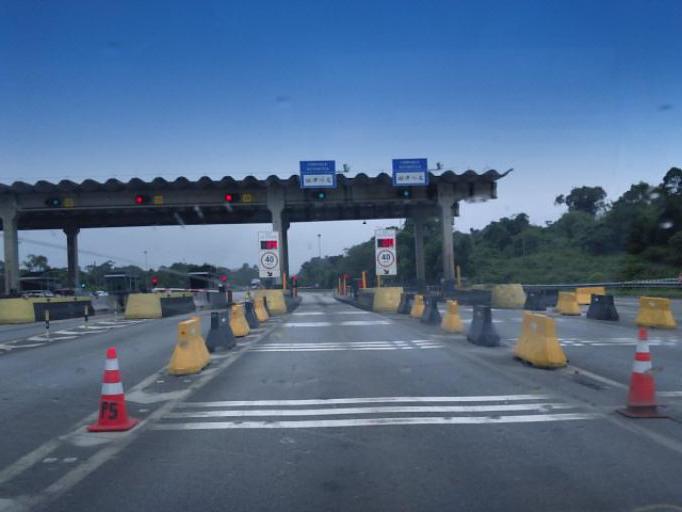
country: BR
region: Sao Paulo
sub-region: Cajati
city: Cajati
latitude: -24.9641
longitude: -48.4124
